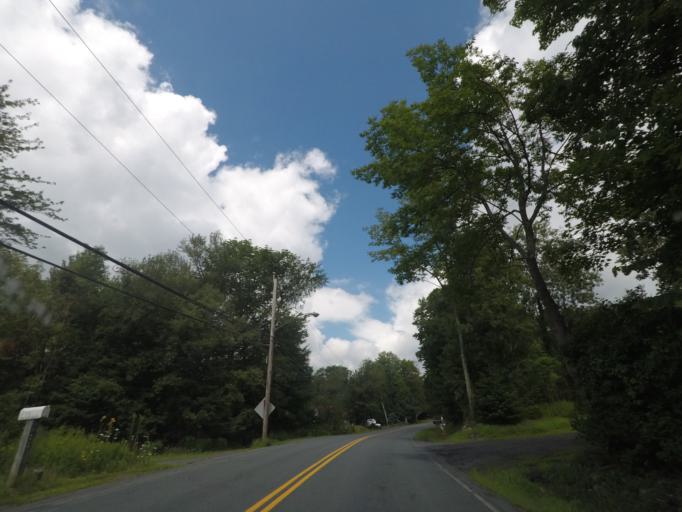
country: US
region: New York
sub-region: Rensselaer County
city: Averill Park
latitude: 42.6464
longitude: -73.4939
